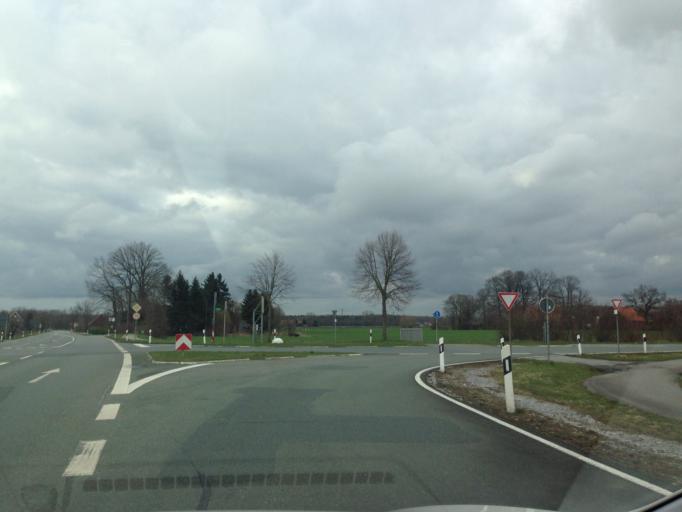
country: DE
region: North Rhine-Westphalia
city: Ludinghausen
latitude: 51.7430
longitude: 7.4757
